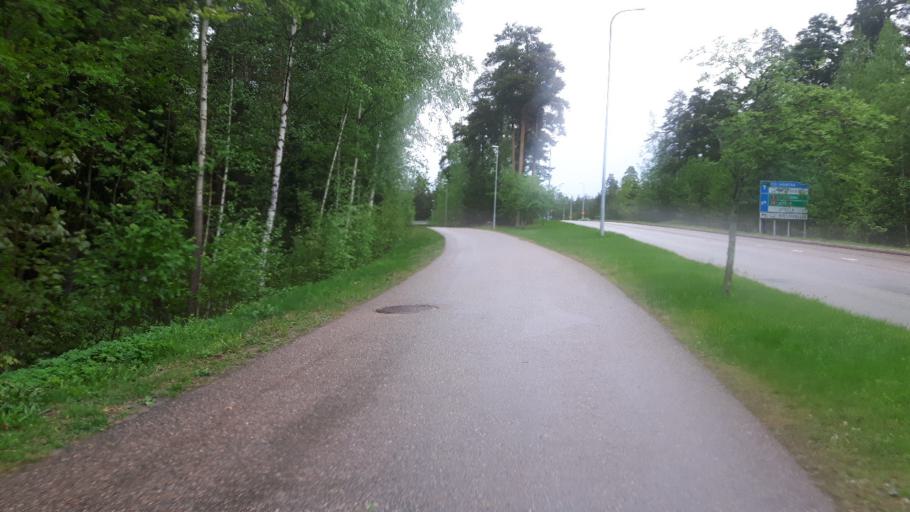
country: FI
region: Kymenlaakso
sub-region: Kotka-Hamina
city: Karhula
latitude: 60.5314
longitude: 26.9542
